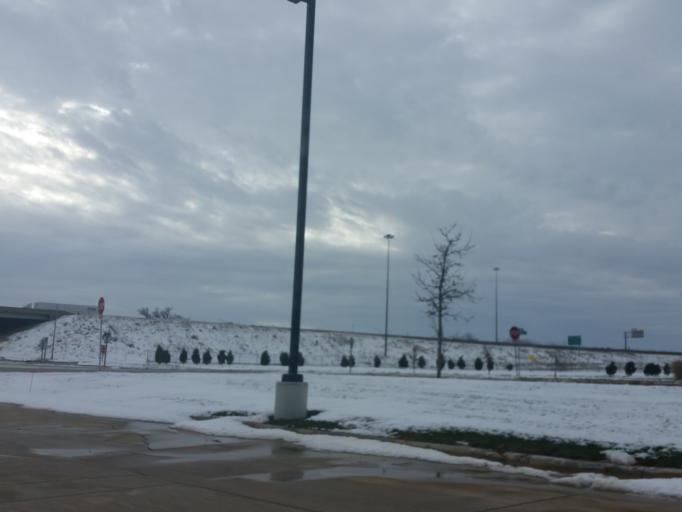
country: US
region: Iowa
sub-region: Black Hawk County
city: Waterloo
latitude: 42.4985
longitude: -92.3540
